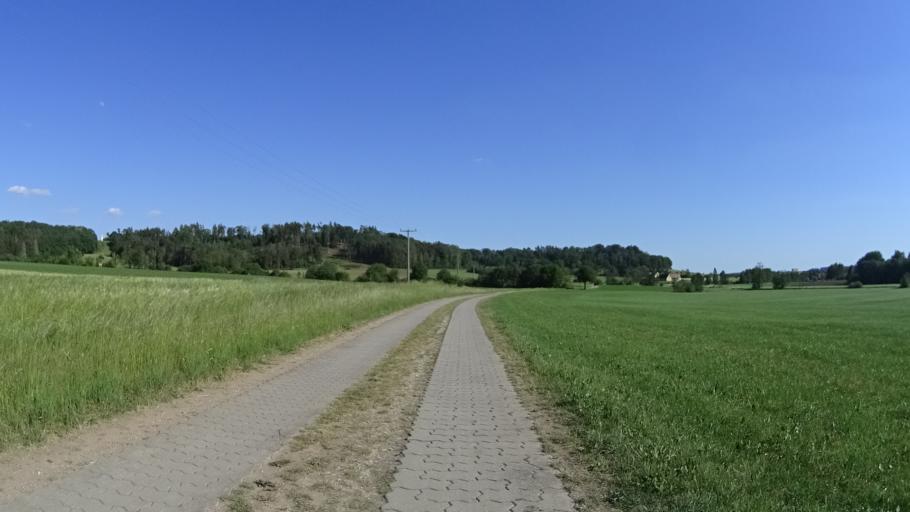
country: DE
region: Bavaria
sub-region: Regierungsbezirk Mittelfranken
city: Feuchtwangen
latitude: 49.1898
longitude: 10.3235
